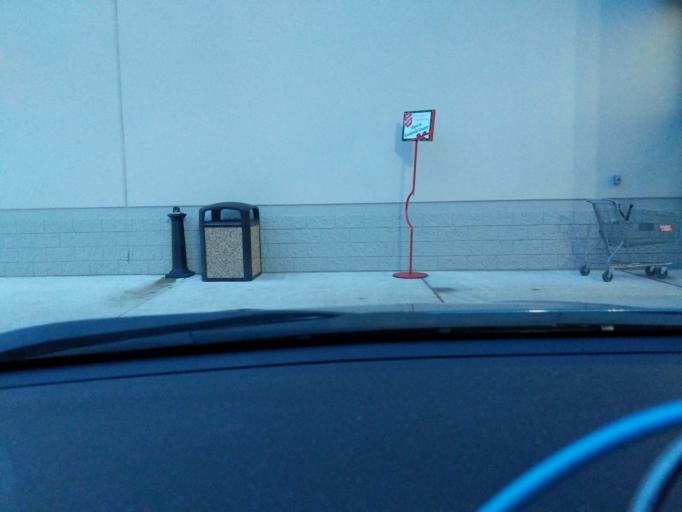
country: US
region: Minnesota
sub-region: Kandiyohi County
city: Willmar
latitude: 45.0944
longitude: -95.0407
